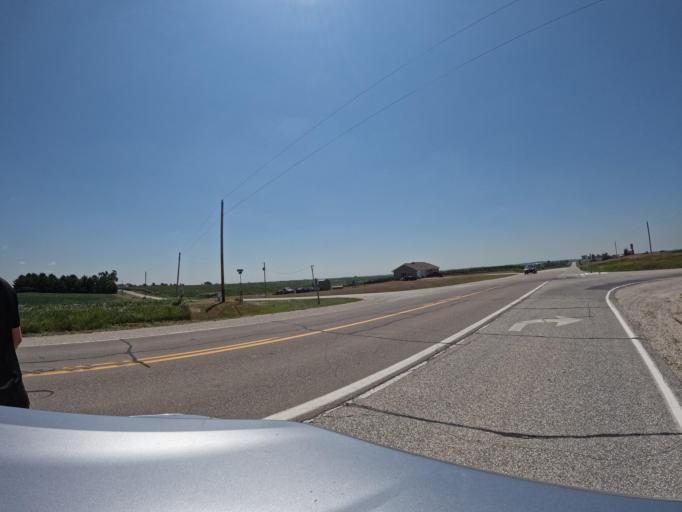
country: US
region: Iowa
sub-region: Keokuk County
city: Sigourney
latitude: 41.2651
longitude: -92.2048
